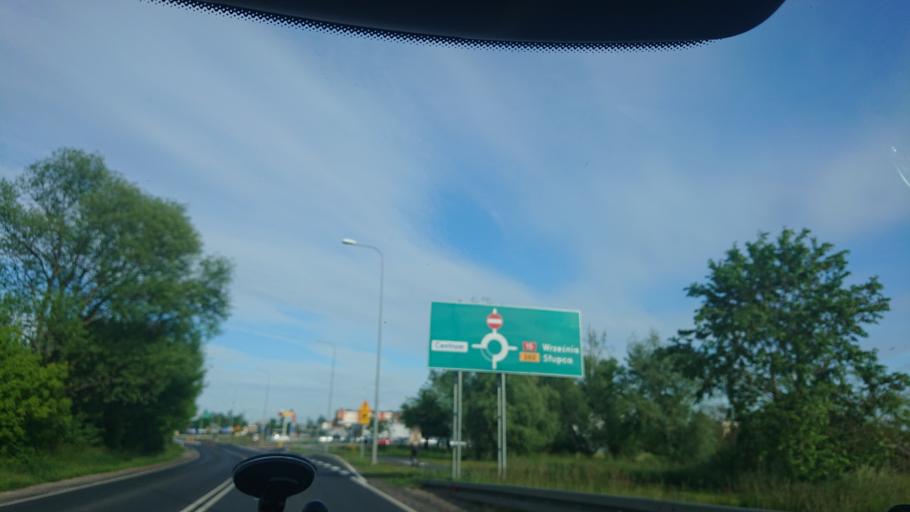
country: PL
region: Greater Poland Voivodeship
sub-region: Powiat gnieznienski
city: Gniezno
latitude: 52.5143
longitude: 17.5915
